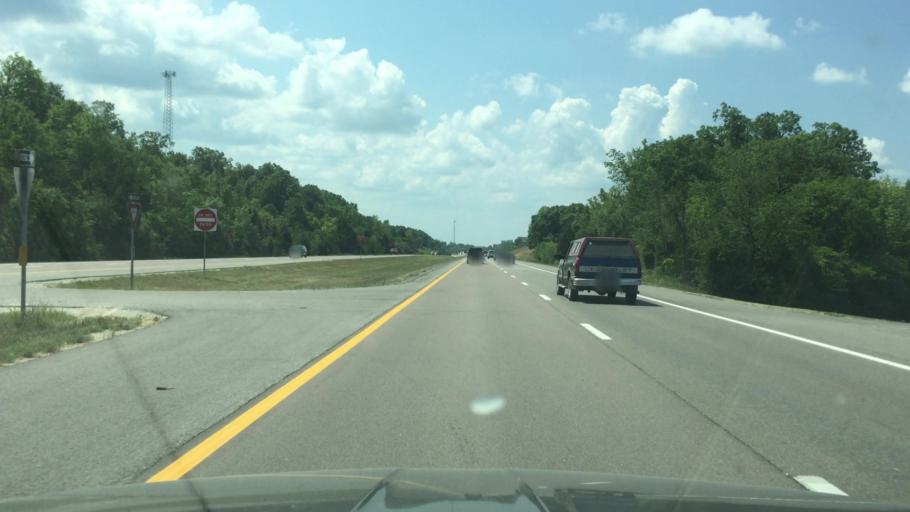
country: US
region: Missouri
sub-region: Miller County
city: Eldon
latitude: 38.2842
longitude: -92.5811
